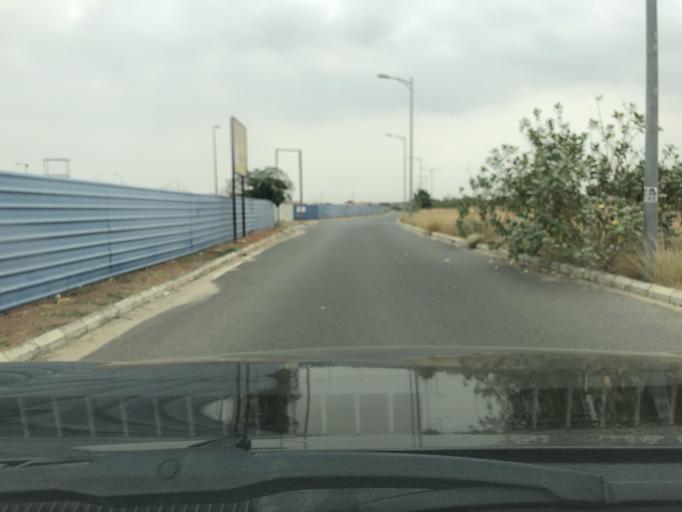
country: AO
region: Luanda
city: Luanda
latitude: -8.9506
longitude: 13.2493
